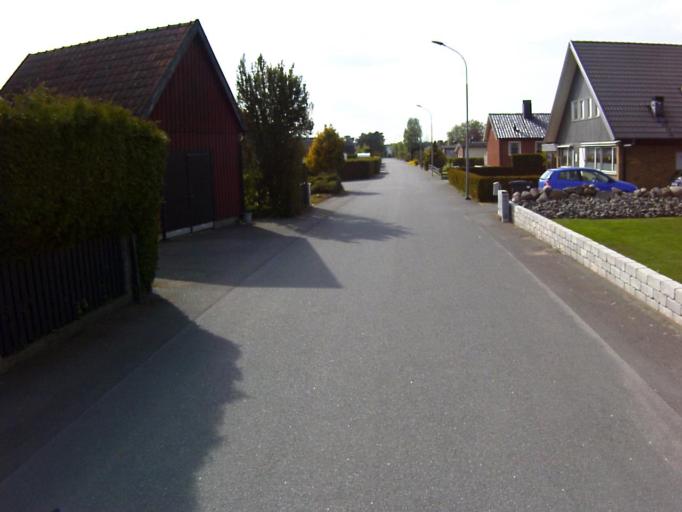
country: SE
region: Skane
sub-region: Kristianstads Kommun
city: Fjalkinge
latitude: 56.0451
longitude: 14.2694
